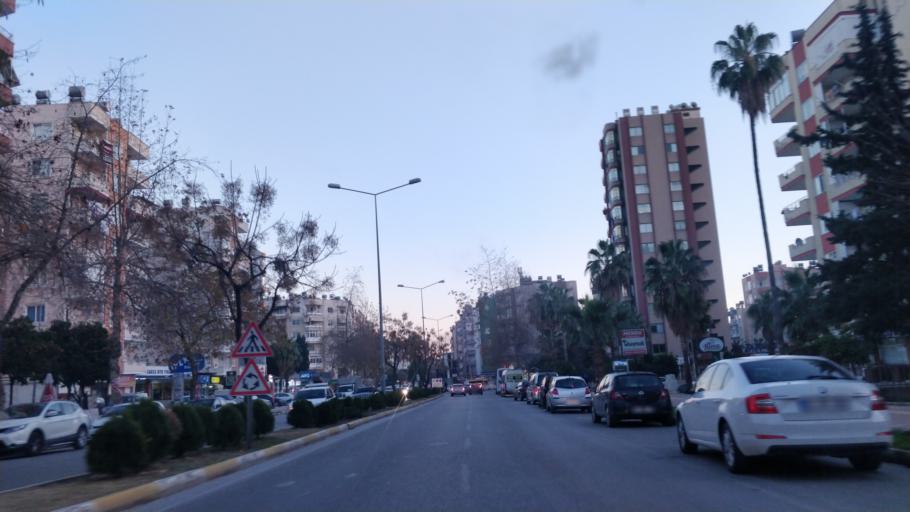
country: TR
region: Mersin
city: Mercin
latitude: 36.7878
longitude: 34.5935
